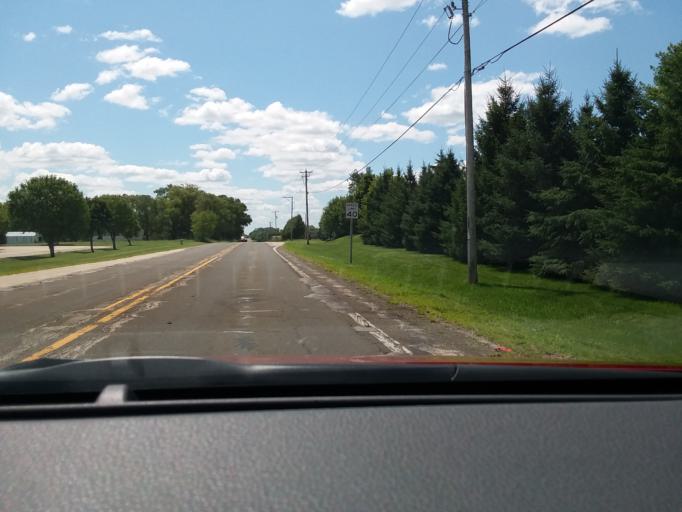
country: US
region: Wisconsin
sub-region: Dane County
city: Windsor
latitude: 43.2307
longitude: -89.3437
